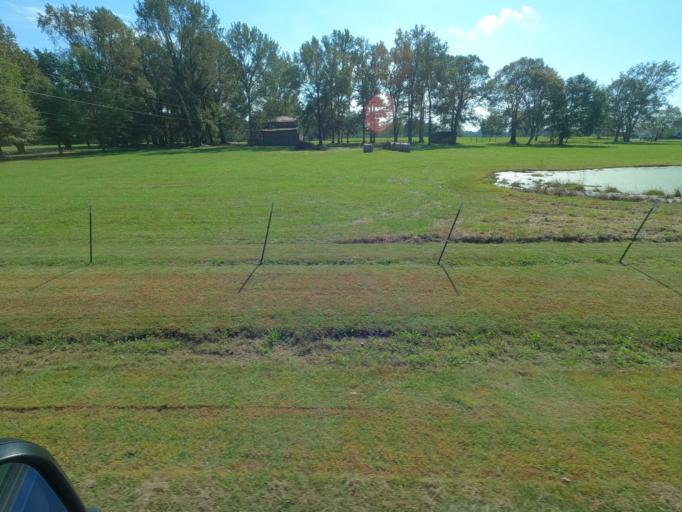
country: US
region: Tennessee
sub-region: Cheatham County
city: Pleasant View
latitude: 36.4426
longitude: -87.1073
